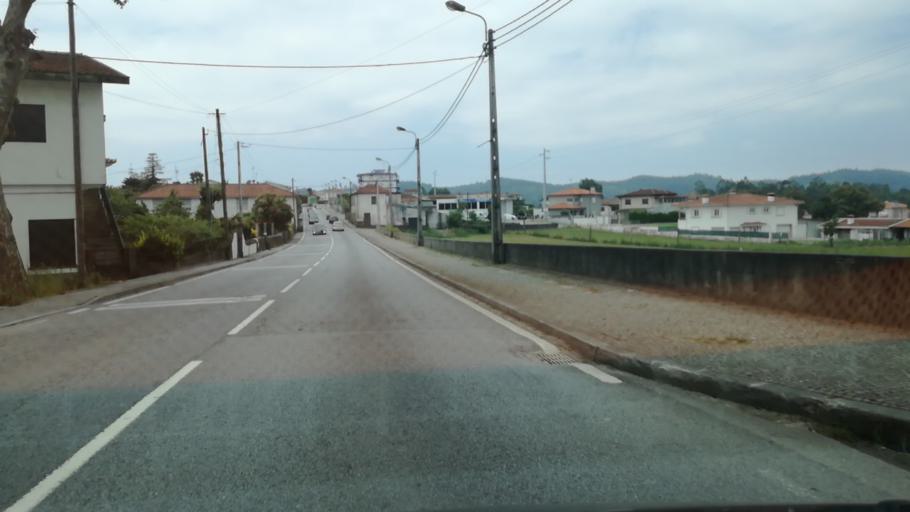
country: PT
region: Porto
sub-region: Trofa
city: Sao Romao do Coronado
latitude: 41.3043
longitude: -8.5895
